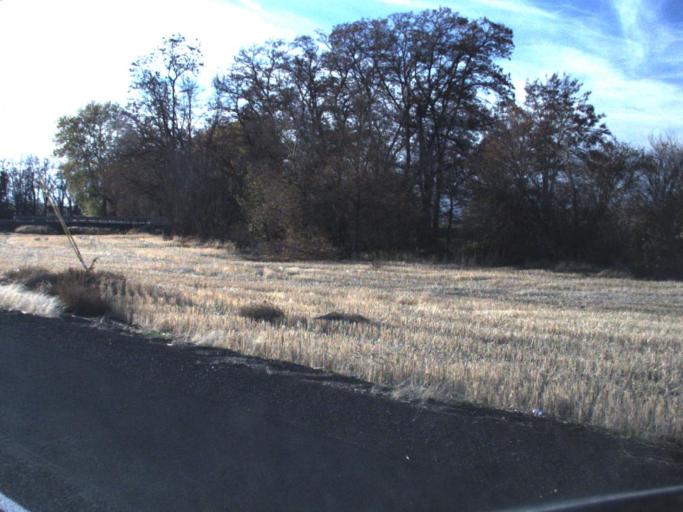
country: US
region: Washington
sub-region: Walla Walla County
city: Walla Walla East
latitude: 46.1193
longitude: -118.2141
